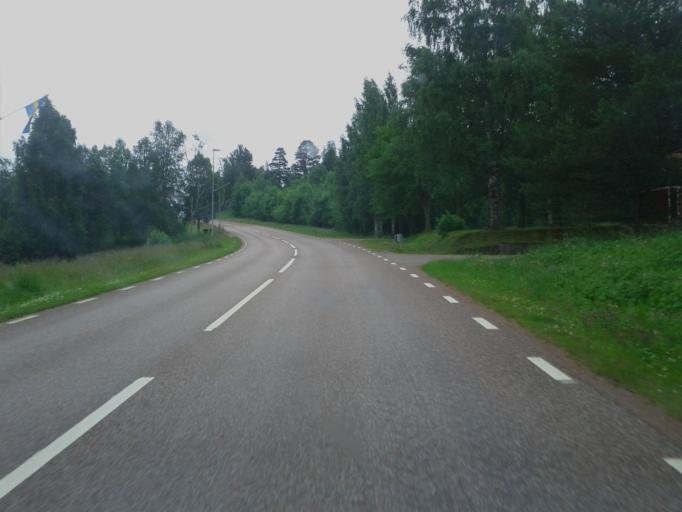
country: NO
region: Hedmark
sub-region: Trysil
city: Innbygda
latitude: 61.6901
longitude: 13.1542
